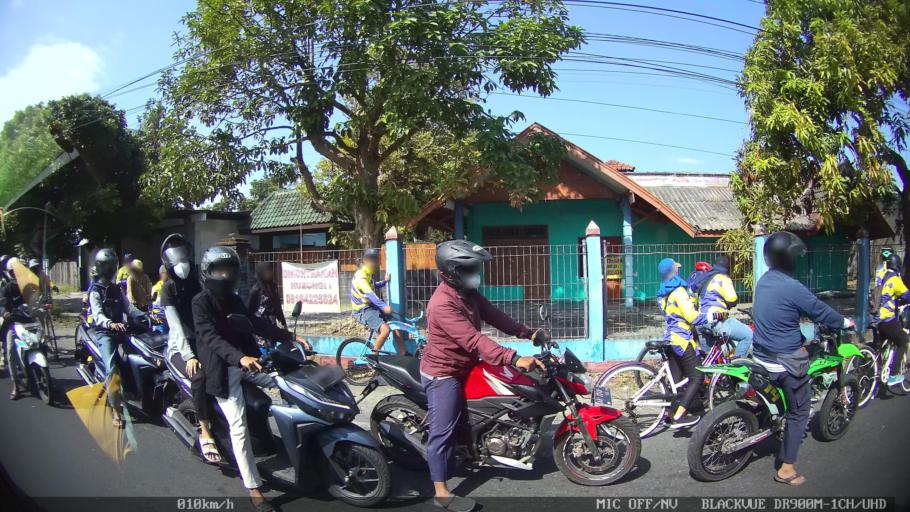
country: ID
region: Daerah Istimewa Yogyakarta
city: Sewon
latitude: -7.8728
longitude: 110.3917
